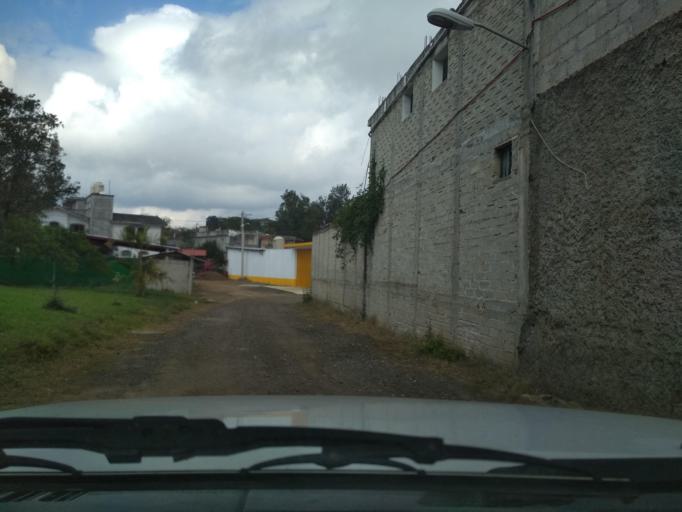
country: MX
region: Veracruz
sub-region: Emiliano Zapata
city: Jacarandas
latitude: 19.4994
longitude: -96.8425
